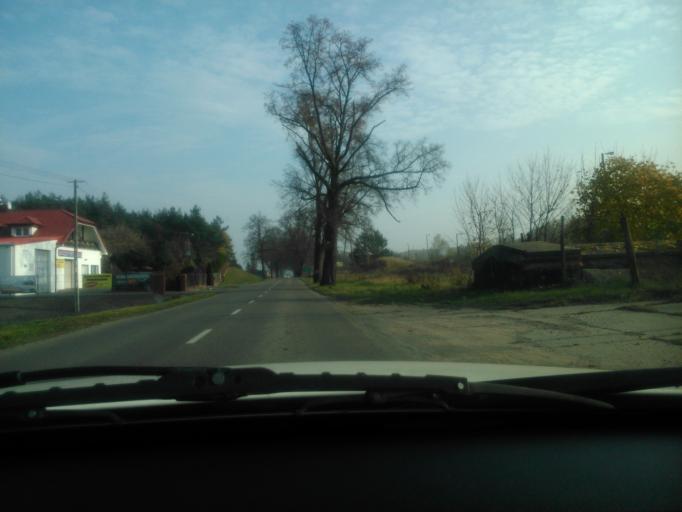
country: PL
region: Warmian-Masurian Voivodeship
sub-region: Powiat dzialdowski
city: Lidzbark
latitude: 53.2617
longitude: 19.8495
